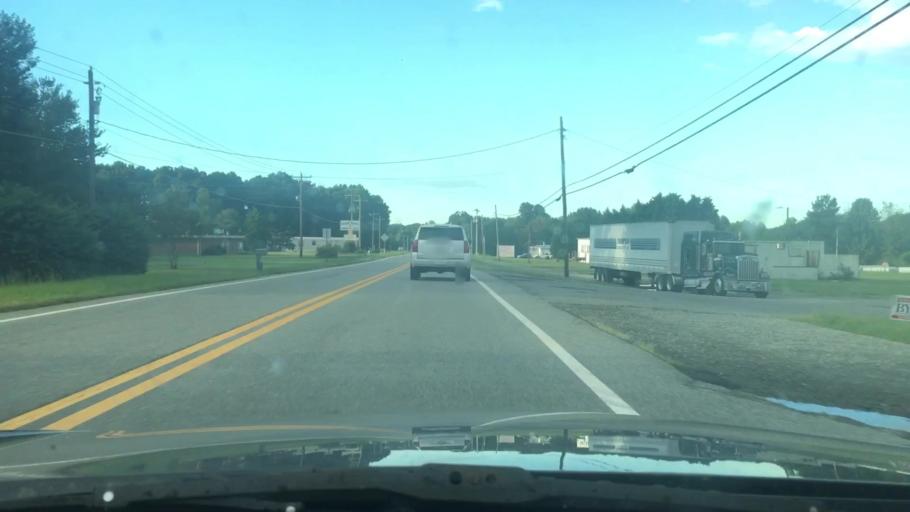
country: US
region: North Carolina
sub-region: Alamance County
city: Green Level
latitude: 36.1544
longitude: -79.3369
